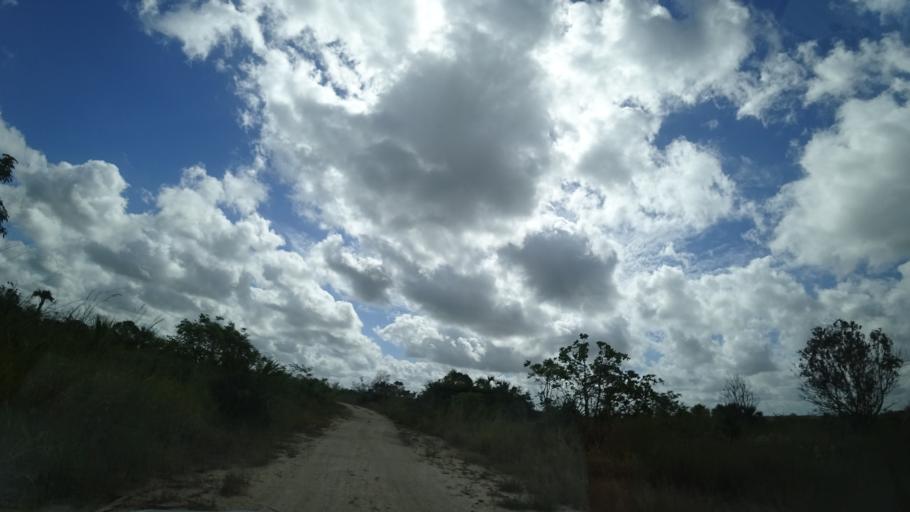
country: MZ
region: Sofala
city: Dondo
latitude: -19.3860
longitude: 34.5924
